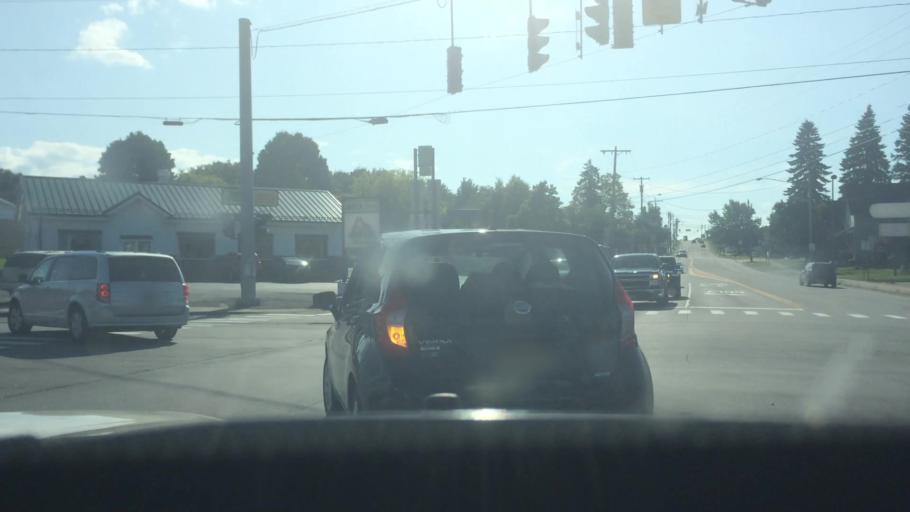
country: US
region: New York
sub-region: Franklin County
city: Malone
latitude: 44.8486
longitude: -74.3007
